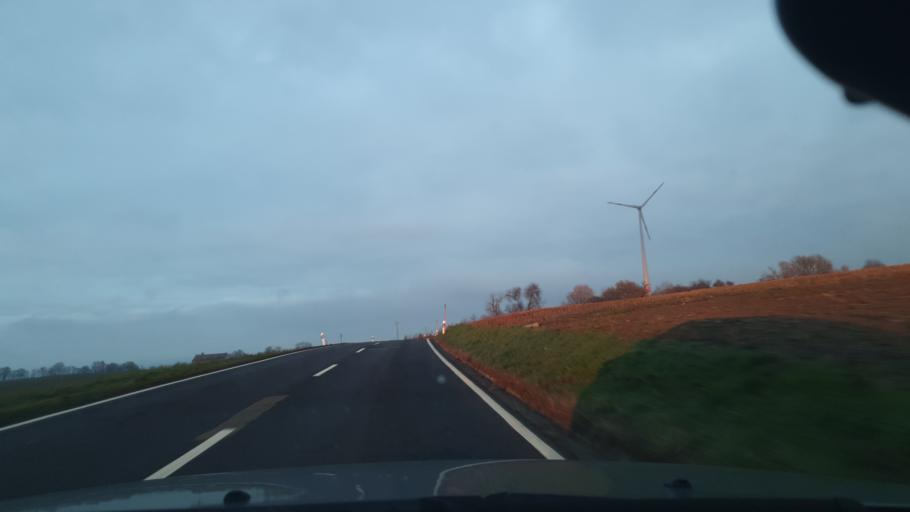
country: DE
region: Rheinland-Pfalz
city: Langwieden
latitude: 49.3742
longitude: 7.5093
